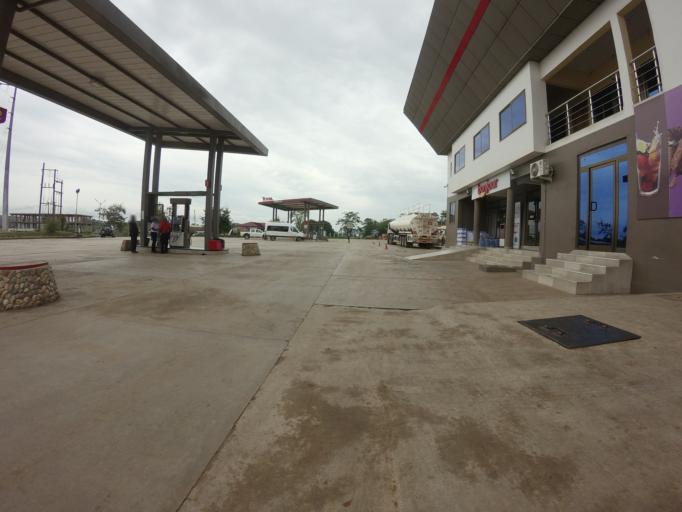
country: GH
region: Eastern
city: Nsawam
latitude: 5.7914
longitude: -0.3386
